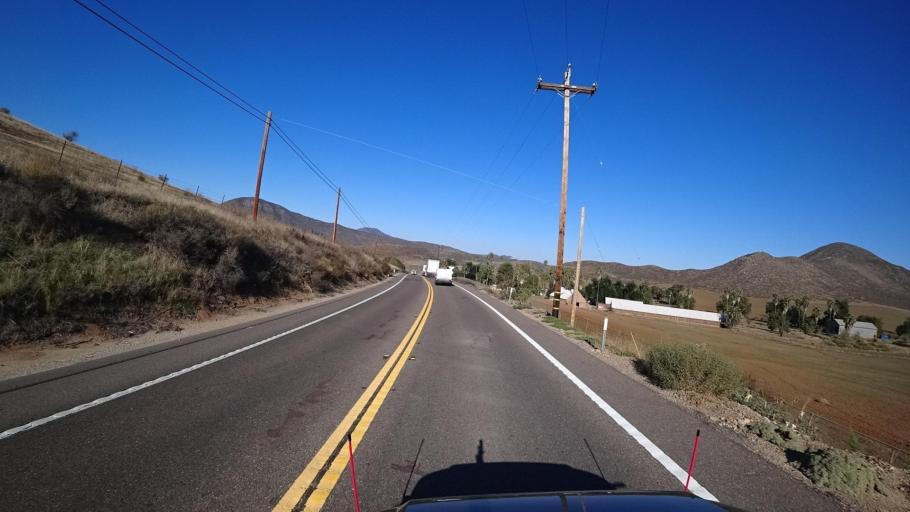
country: US
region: California
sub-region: San Diego County
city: Jamul
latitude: 32.6834
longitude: -116.8426
